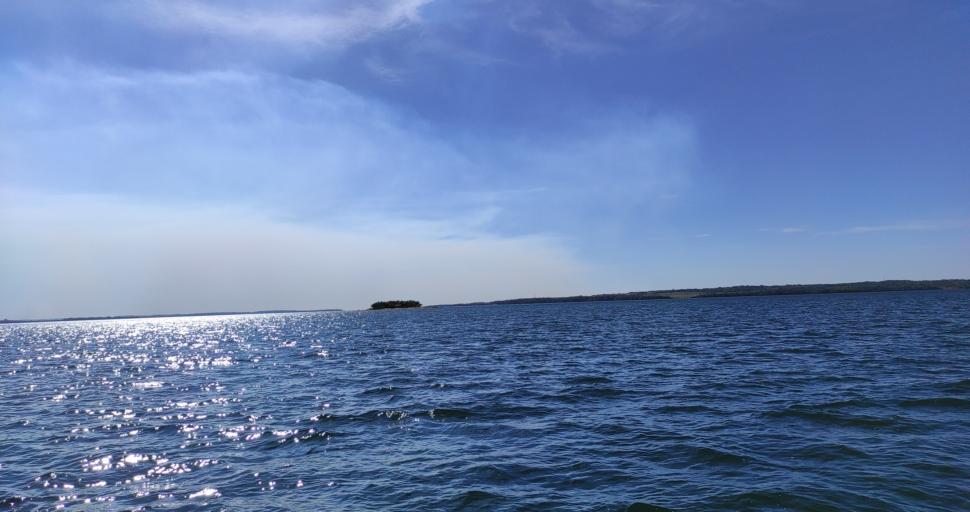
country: AR
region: Misiones
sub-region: Departamento de Capital
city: Posadas
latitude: -27.3436
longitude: -55.9395
